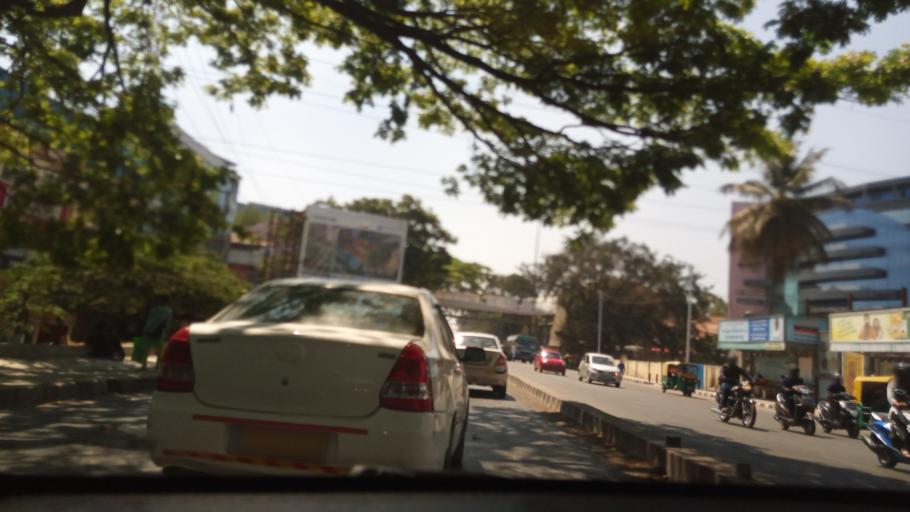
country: IN
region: Karnataka
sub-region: Bangalore Urban
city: Bangalore
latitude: 12.9331
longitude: 77.6130
